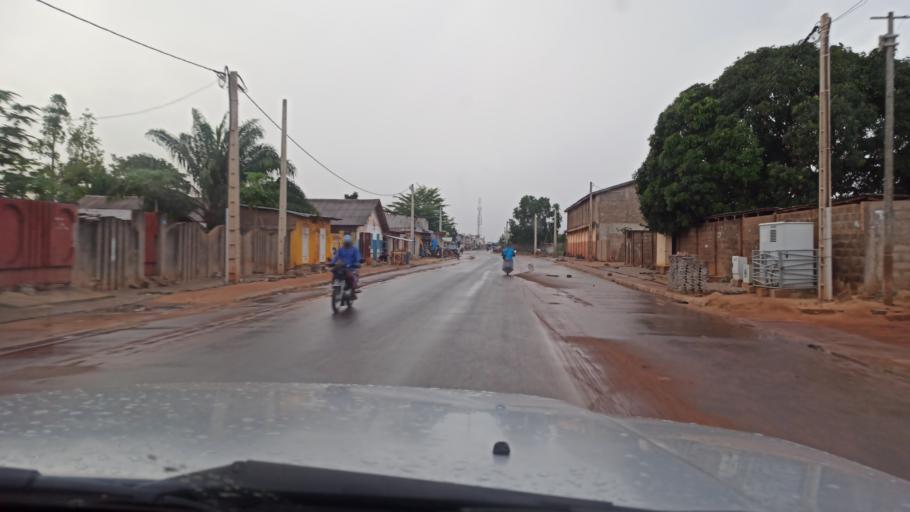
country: BJ
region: Queme
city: Porto-Novo
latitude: 6.4947
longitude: 2.6439
